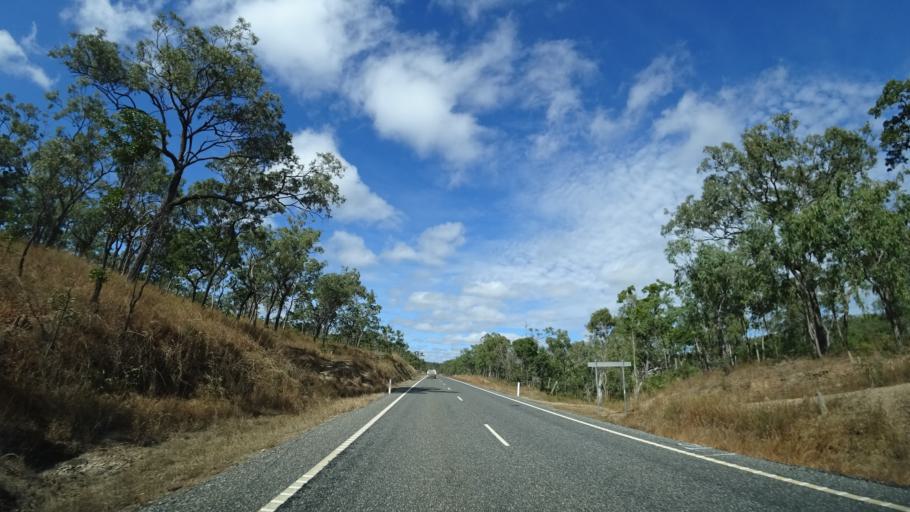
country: AU
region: Queensland
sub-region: Cairns
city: Port Douglas
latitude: -16.2798
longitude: 144.7142
